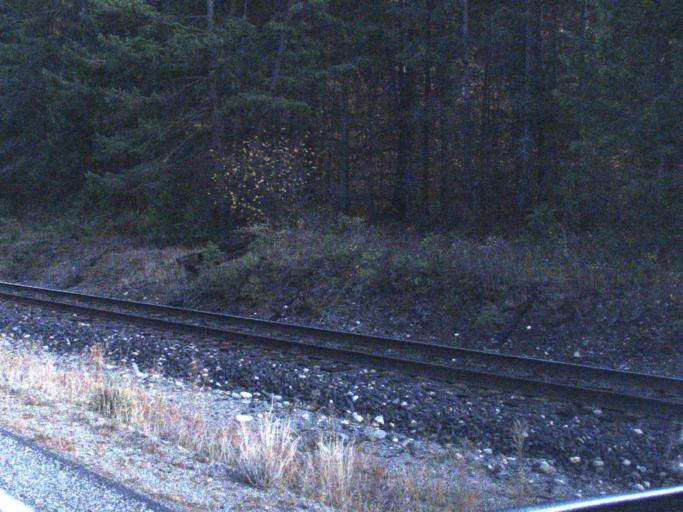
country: US
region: Washington
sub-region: Stevens County
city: Kettle Falls
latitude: 48.8141
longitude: -117.9656
